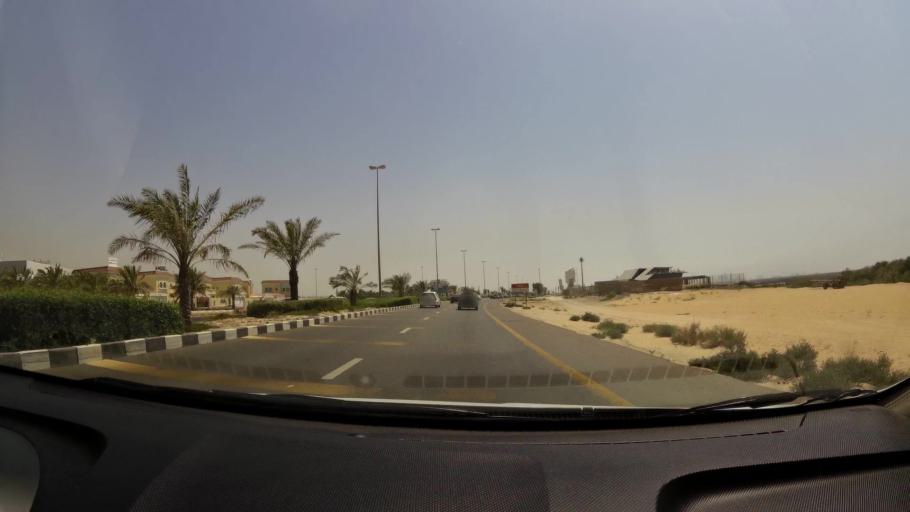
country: AE
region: Ajman
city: Ajman
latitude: 25.4269
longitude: 55.5006
